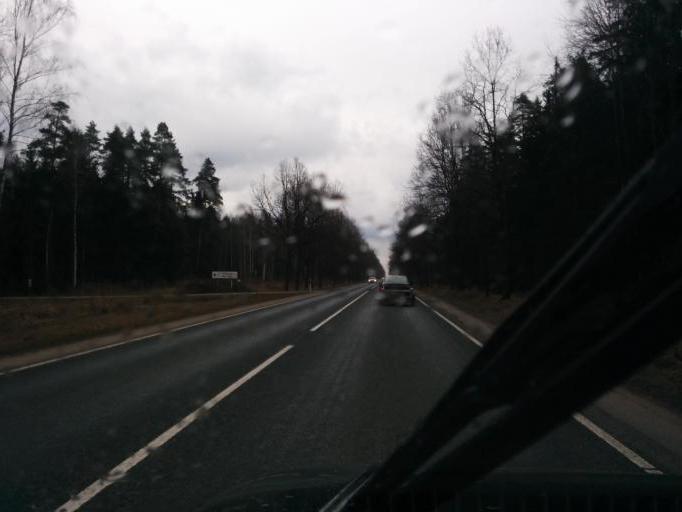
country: LV
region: Ozolnieku
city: Ozolnieki
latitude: 56.7001
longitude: 23.8108
